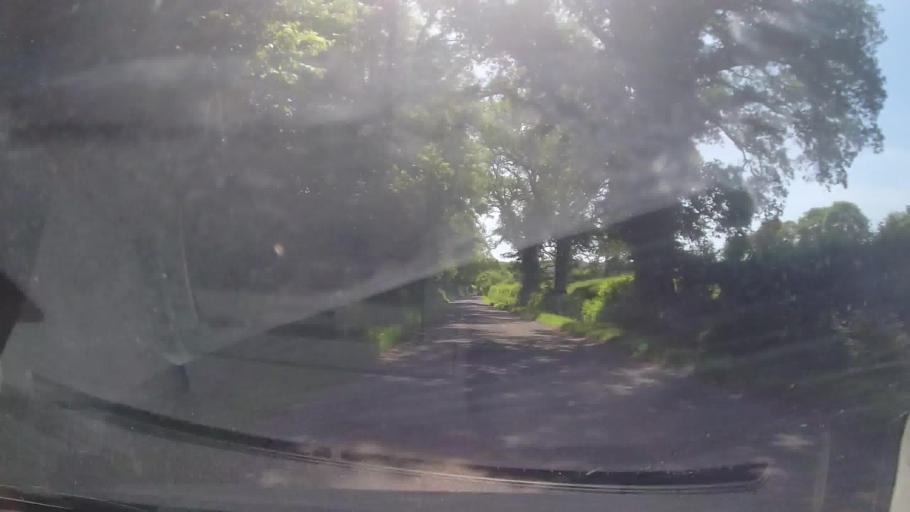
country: GB
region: England
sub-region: Herefordshire
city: Llanrothal
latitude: 51.8637
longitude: -2.7327
